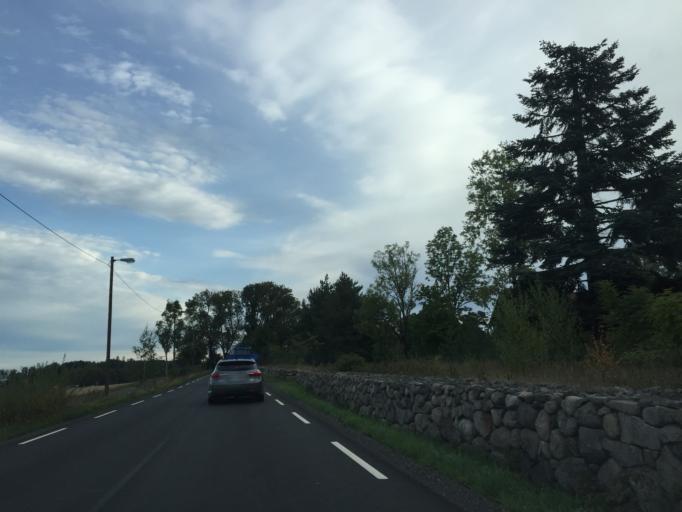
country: NO
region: Akershus
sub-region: As
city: As
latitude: 59.7132
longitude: 10.7733
